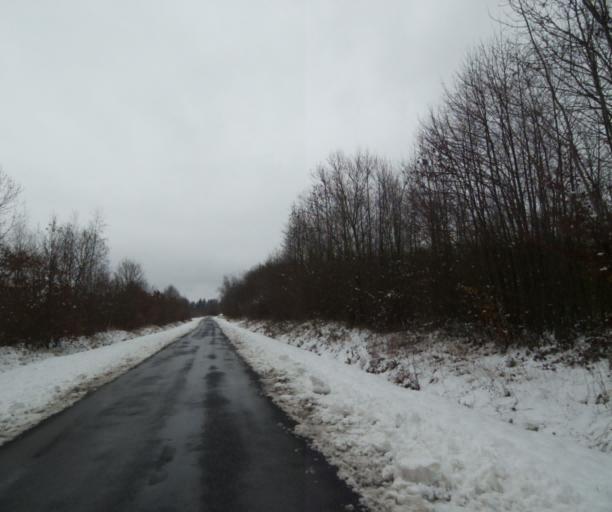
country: FR
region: Champagne-Ardenne
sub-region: Departement de la Haute-Marne
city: Laneuville-a-Remy
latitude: 48.4677
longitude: 4.8692
